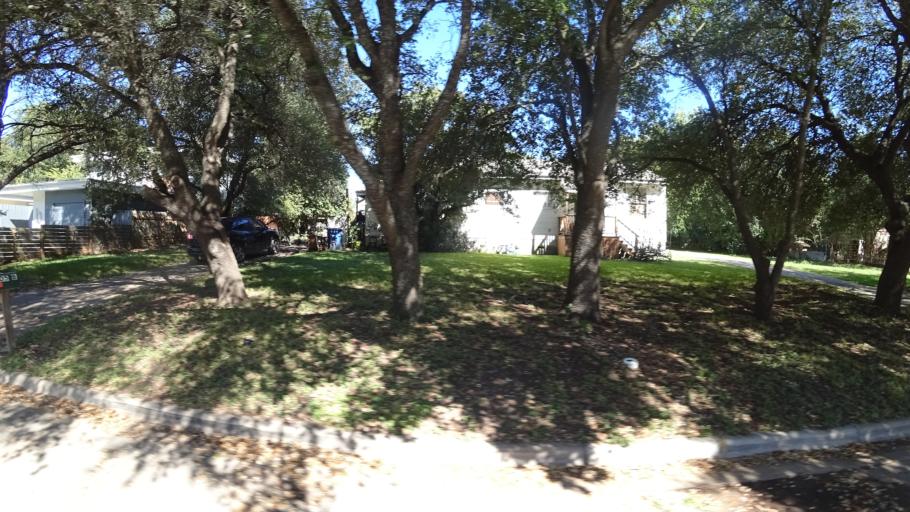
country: US
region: Texas
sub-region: Travis County
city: Austin
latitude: 30.2866
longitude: -97.7006
